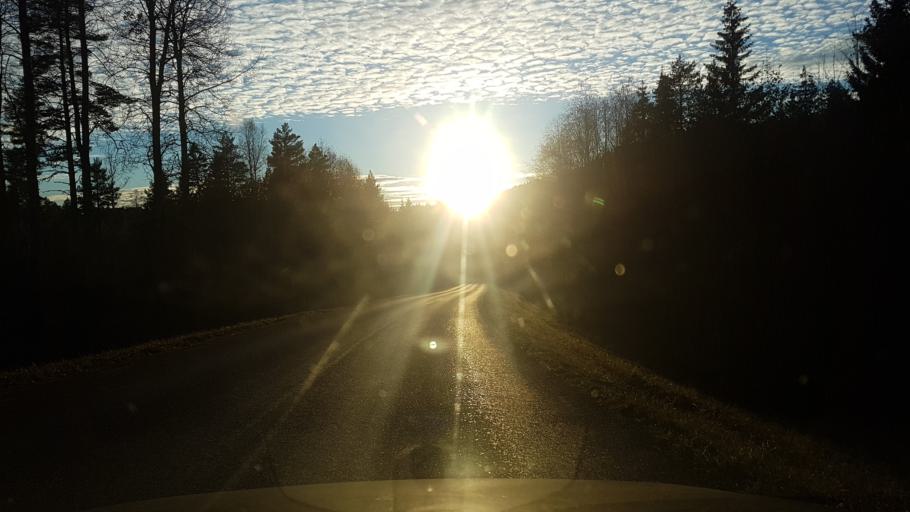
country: SE
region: Dalarna
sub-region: Leksand Municipality
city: Smedby
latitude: 60.7259
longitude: 15.1249
